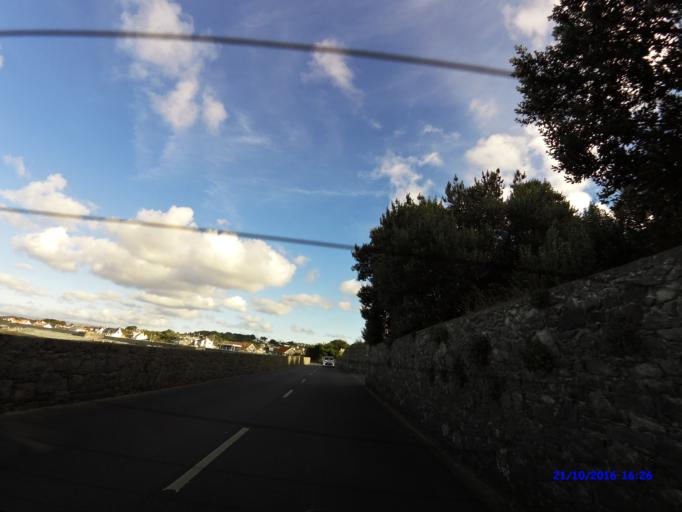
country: GG
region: St Peter Port
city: Saint Peter Port
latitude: 49.4587
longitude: -2.6384
